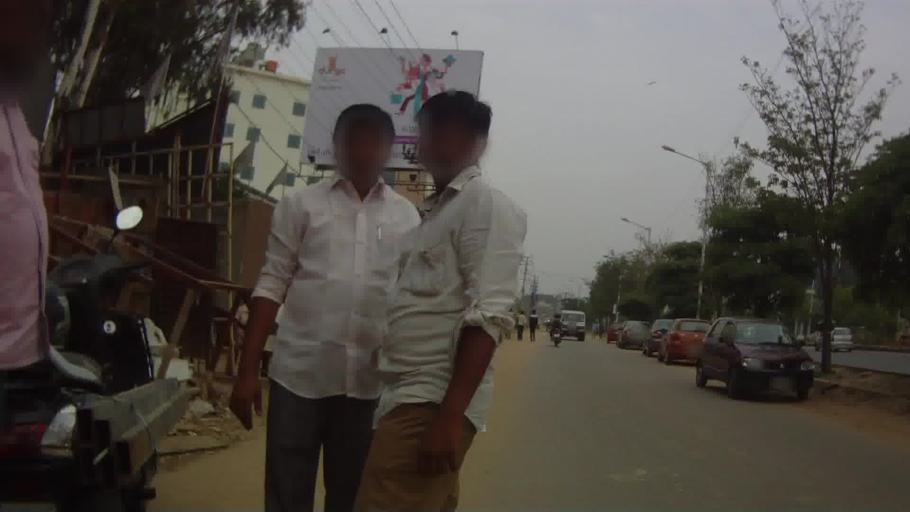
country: IN
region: Karnataka
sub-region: Bangalore Urban
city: Bangalore
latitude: 12.9760
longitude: 77.6971
